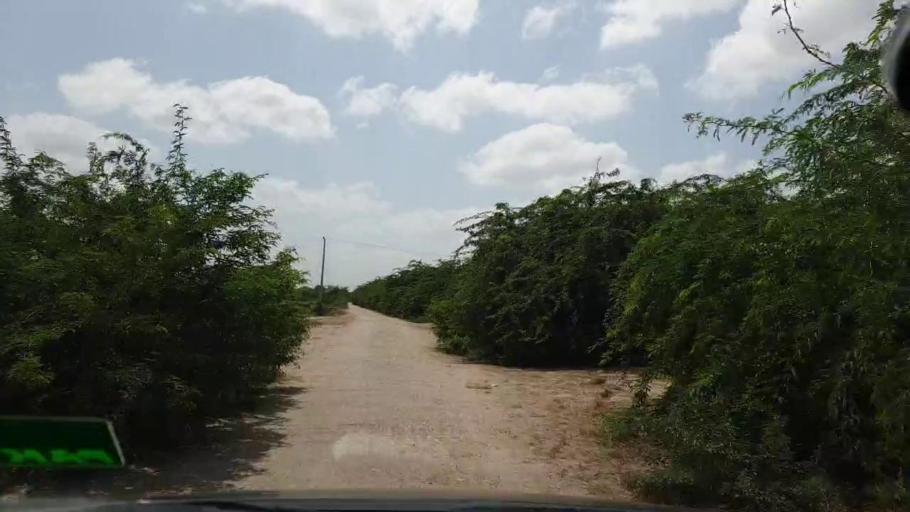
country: PK
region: Sindh
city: Kadhan
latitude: 24.5663
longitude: 69.2110
